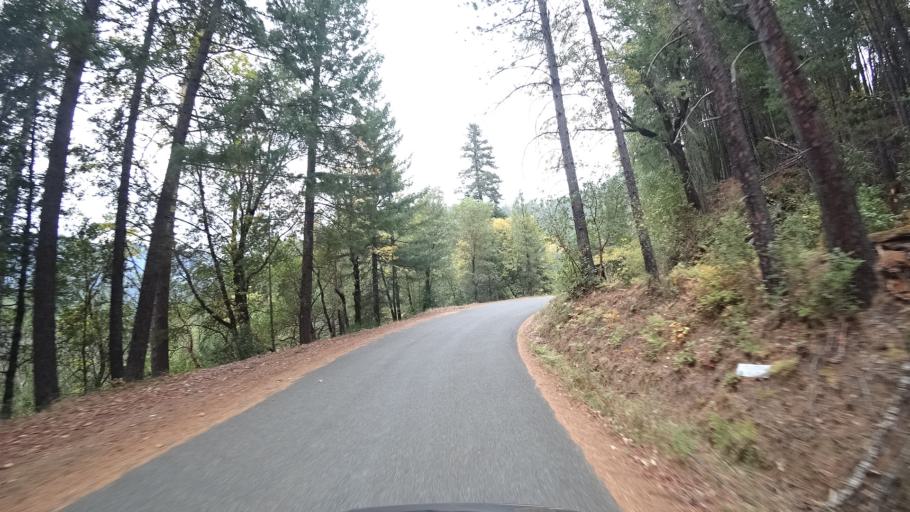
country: US
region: California
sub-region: Siskiyou County
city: Happy Camp
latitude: 41.7767
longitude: -123.3817
